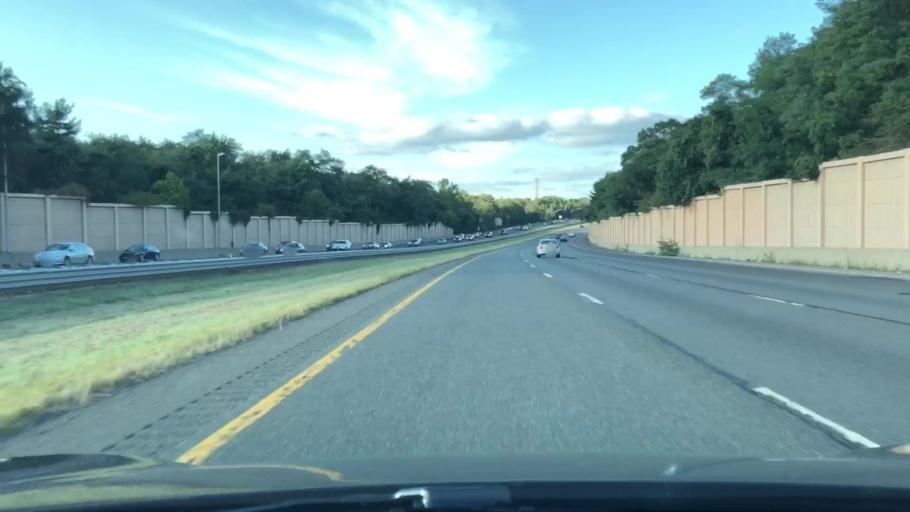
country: US
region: New Jersey
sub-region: Mercer County
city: Mercerville
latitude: 40.2363
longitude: -74.7014
